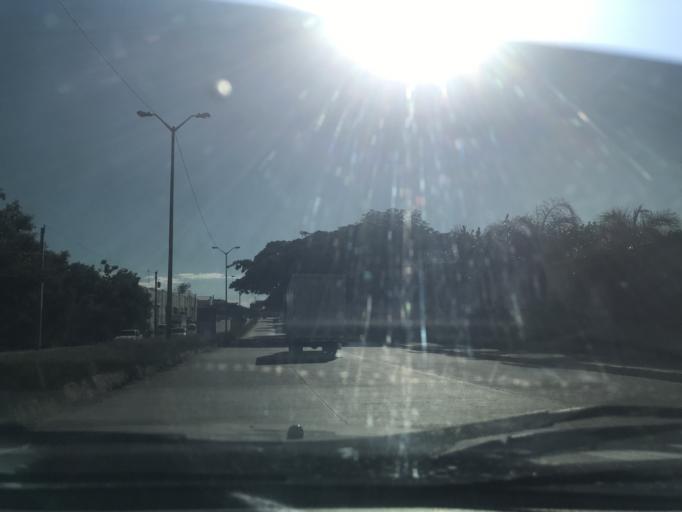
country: DO
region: Santiago
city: Santiago de los Caballeros
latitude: 19.4256
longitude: -70.6784
